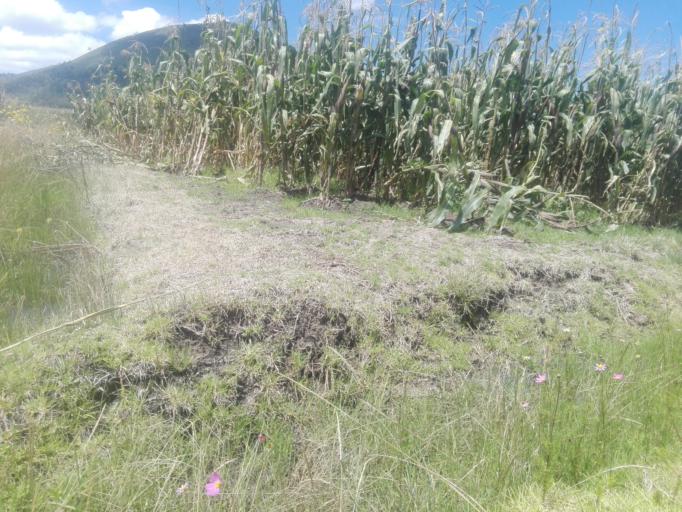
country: MX
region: Mexico
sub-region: Jocotitlan
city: Concepcion Caro
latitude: 19.7622
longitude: -99.9005
